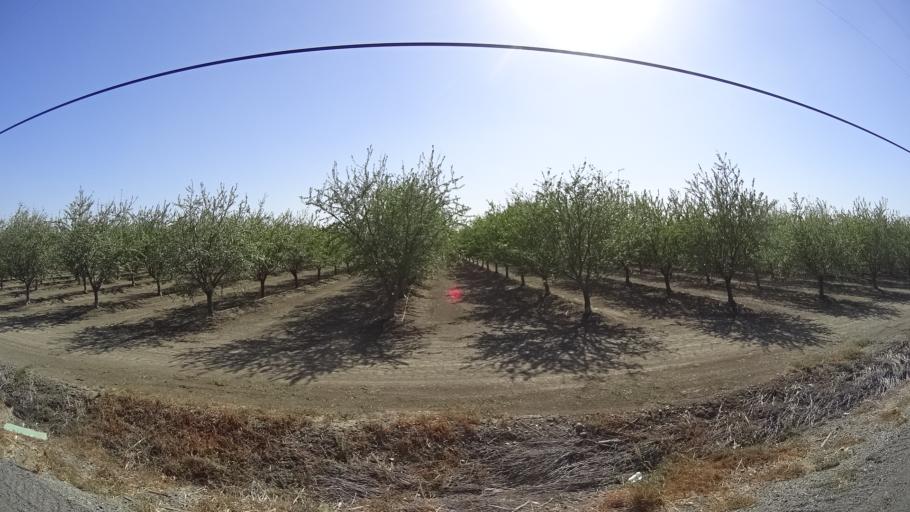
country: US
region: California
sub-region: Yolo County
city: Davis
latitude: 38.5901
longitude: -121.7553
